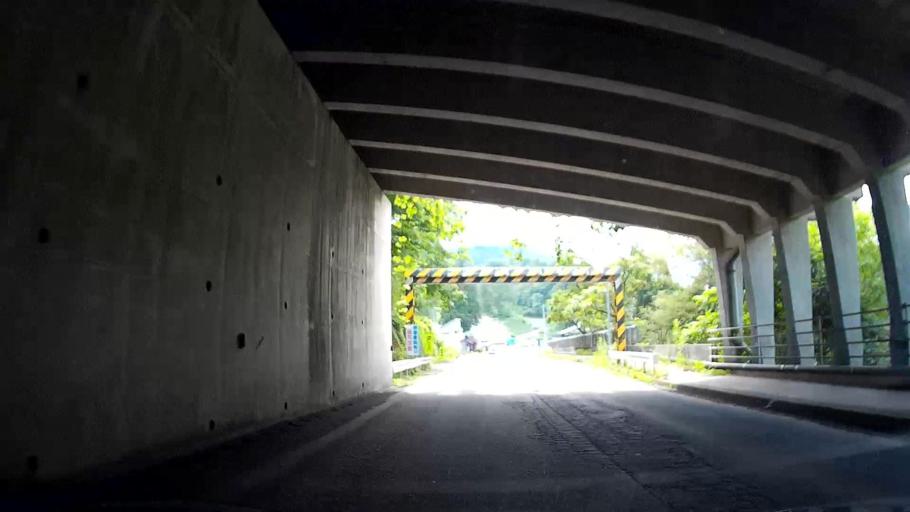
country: JP
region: Niigata
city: Tokamachi
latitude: 36.9960
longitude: 138.6159
